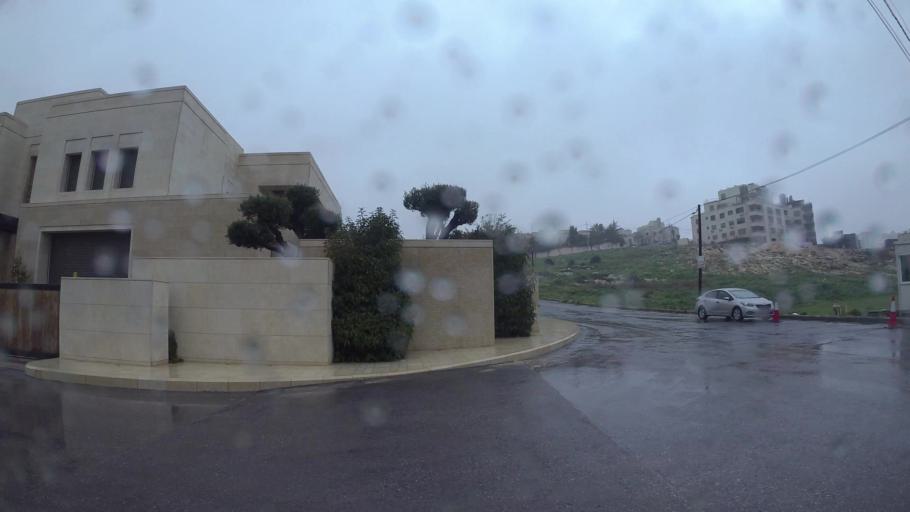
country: JO
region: Amman
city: Wadi as Sir
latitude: 31.9941
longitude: 35.8280
